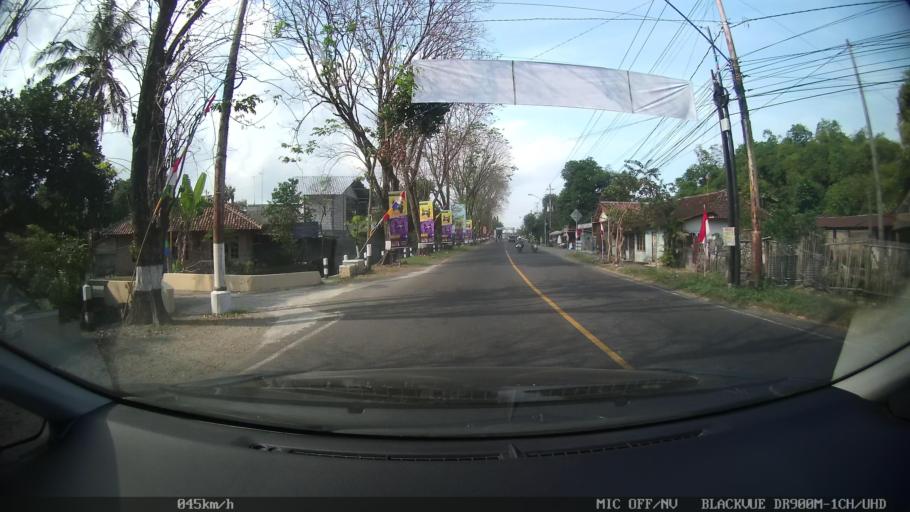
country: ID
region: Daerah Istimewa Yogyakarta
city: Kasihan
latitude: -7.8417
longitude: 110.3469
